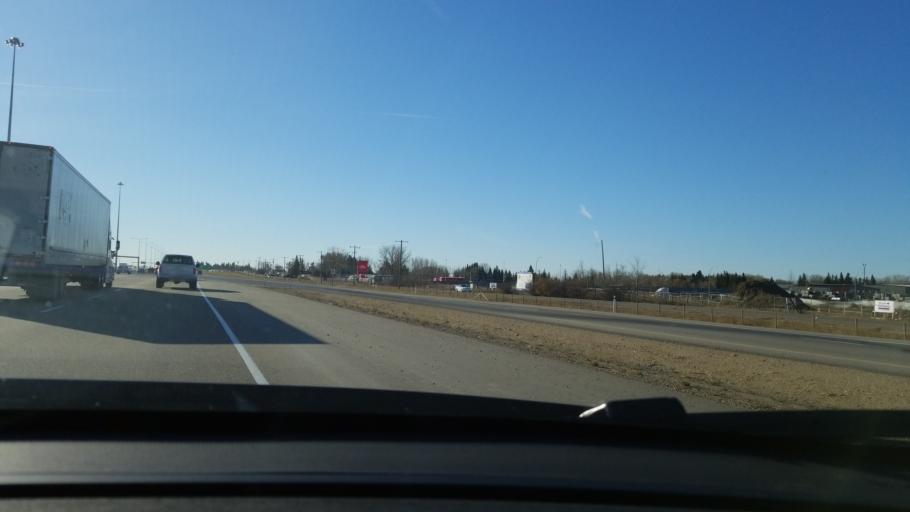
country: CA
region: Alberta
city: Sherwood Park
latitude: 53.5071
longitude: -113.3445
